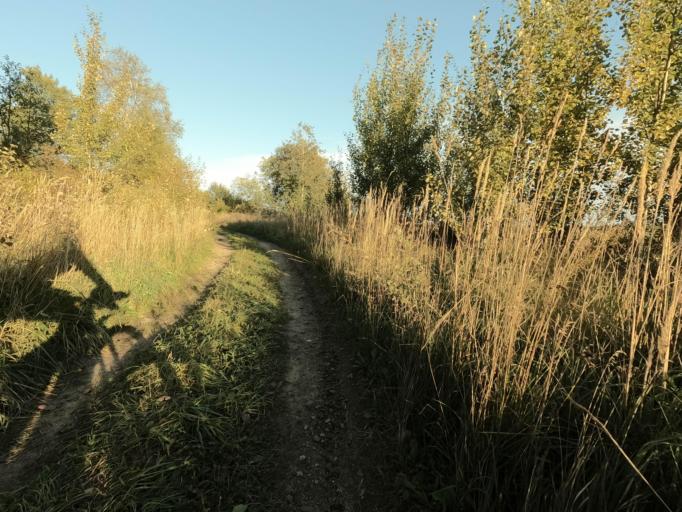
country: RU
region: Leningrad
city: Nikol'skoye
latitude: 59.7006
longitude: 30.7435
